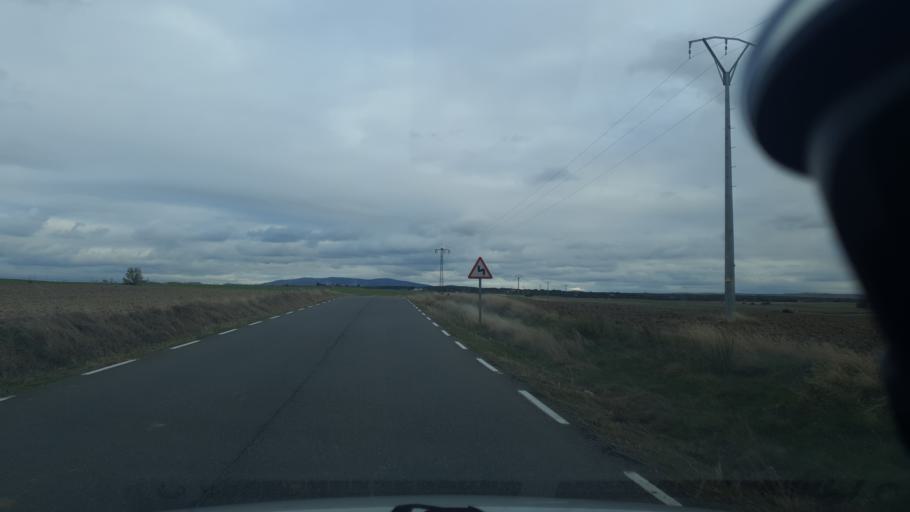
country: ES
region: Castille and Leon
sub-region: Provincia de Avila
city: Velayos
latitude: 40.8369
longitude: -4.6184
